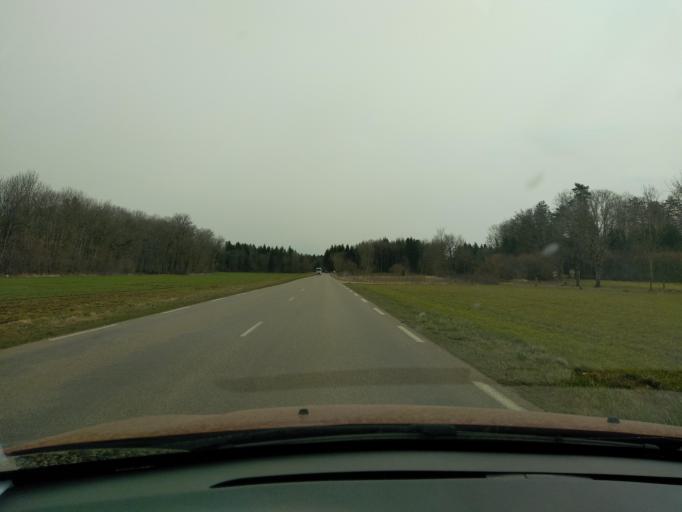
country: FR
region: Franche-Comte
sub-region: Departement du Jura
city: Champagnole
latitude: 46.7517
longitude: 5.8344
